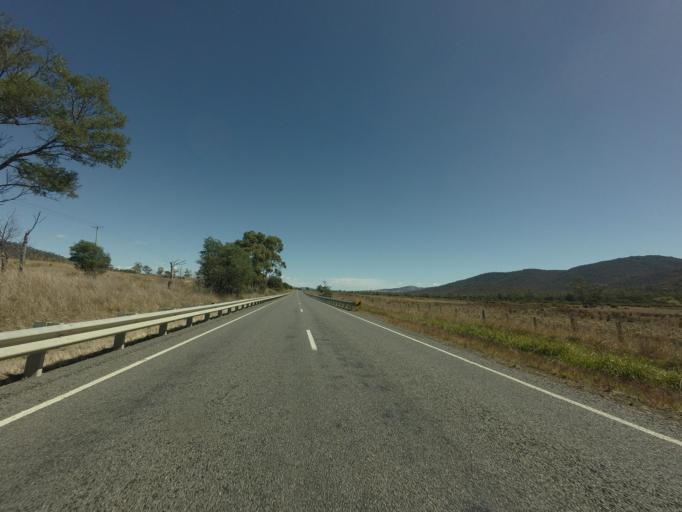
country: AU
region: Tasmania
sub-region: Northern Midlands
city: Evandale
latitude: -41.7431
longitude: 147.7894
